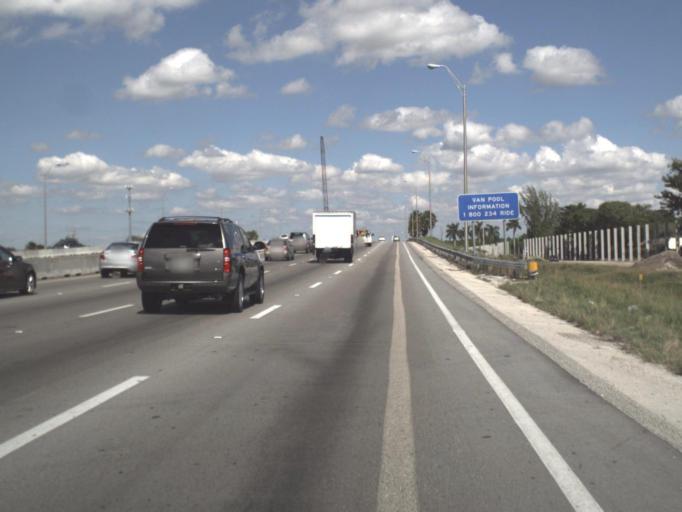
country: US
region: Florida
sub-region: Miami-Dade County
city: South Miami Heights
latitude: 25.6095
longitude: -80.3780
